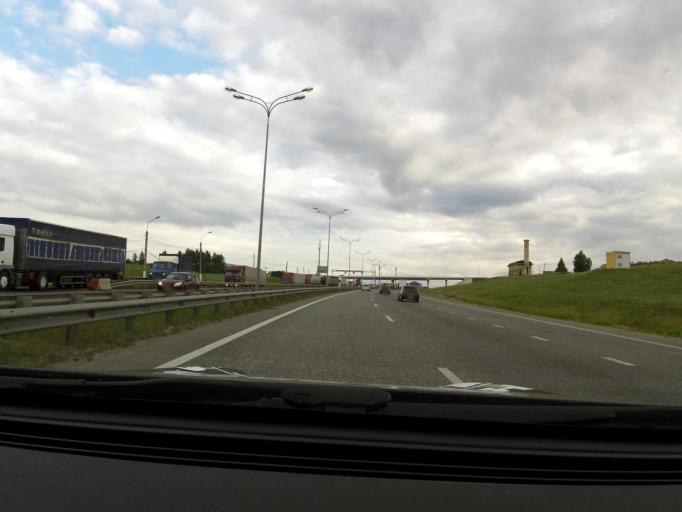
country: RU
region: Tatarstan
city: Osinovo
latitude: 55.7766
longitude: 48.8398
